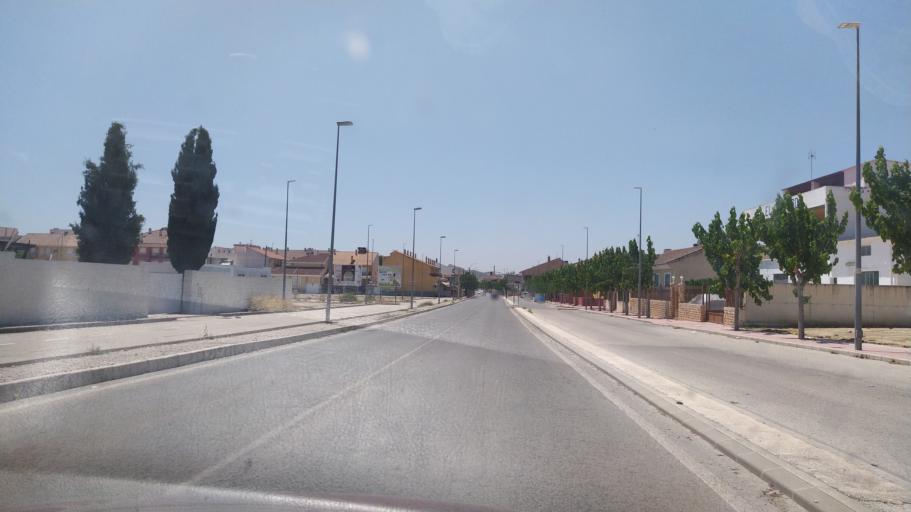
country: ES
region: Murcia
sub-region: Murcia
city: Ceuti
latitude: 38.0875
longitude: -1.2765
